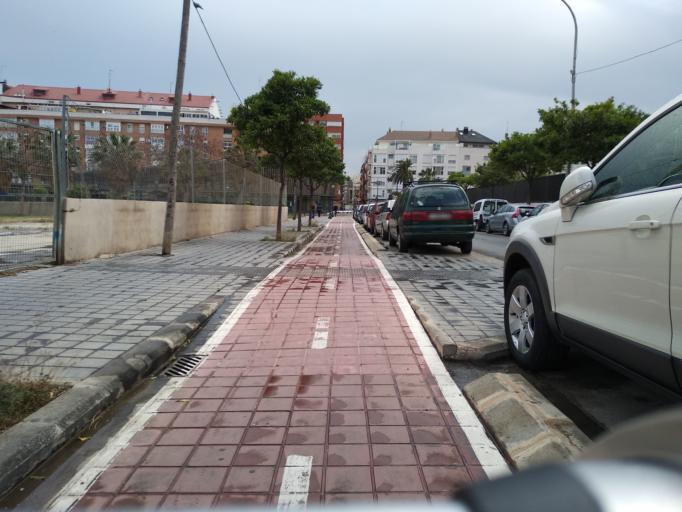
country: ES
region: Valencia
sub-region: Provincia de Valencia
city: Alboraya
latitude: 39.4656
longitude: -0.3378
